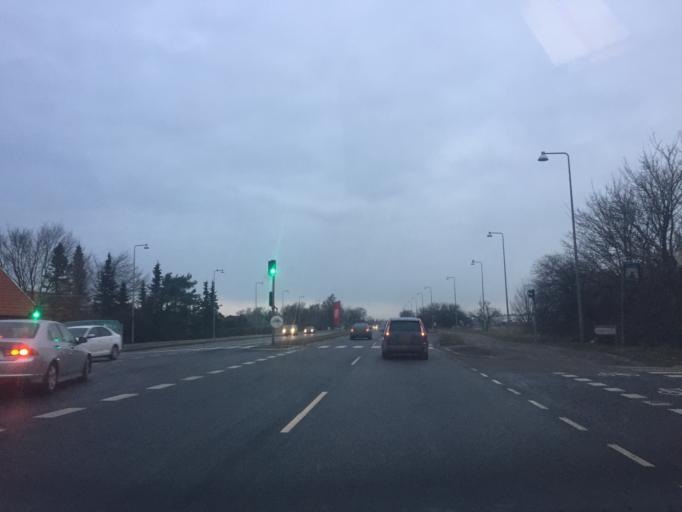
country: DK
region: Zealand
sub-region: Koge Kommune
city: Koge
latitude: 55.4920
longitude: 12.1913
